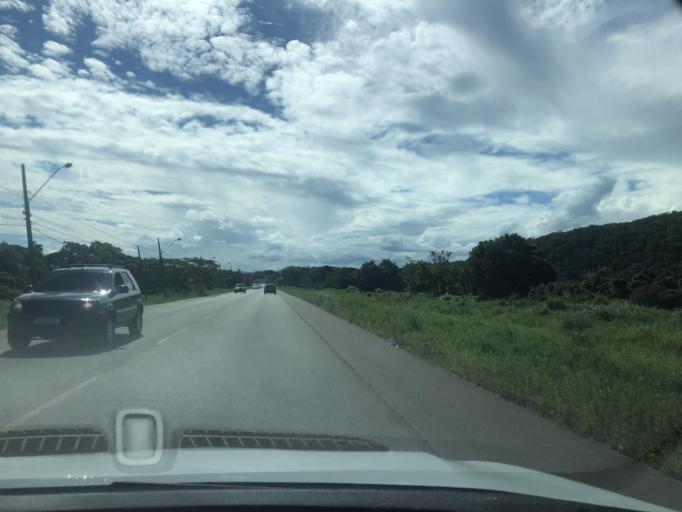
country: BR
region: Santa Catarina
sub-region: Sao Francisco Do Sul
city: Sao Francisco do Sul
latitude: -26.2062
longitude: -48.5320
